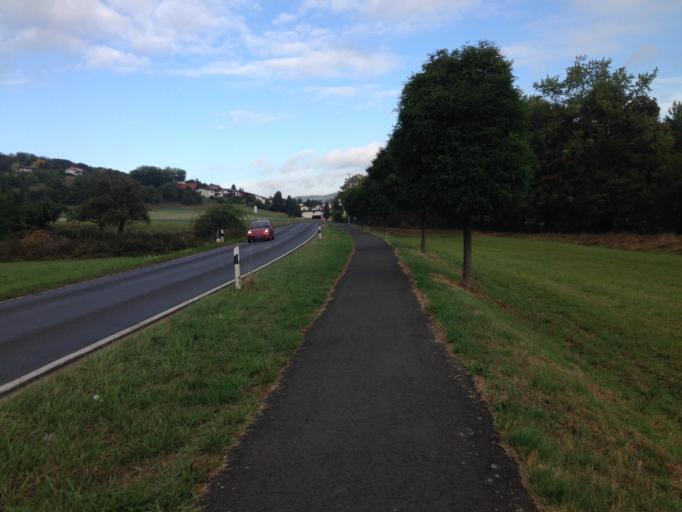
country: DE
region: Hesse
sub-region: Regierungsbezirk Giessen
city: Heuchelheim
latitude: 50.6196
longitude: 8.5908
